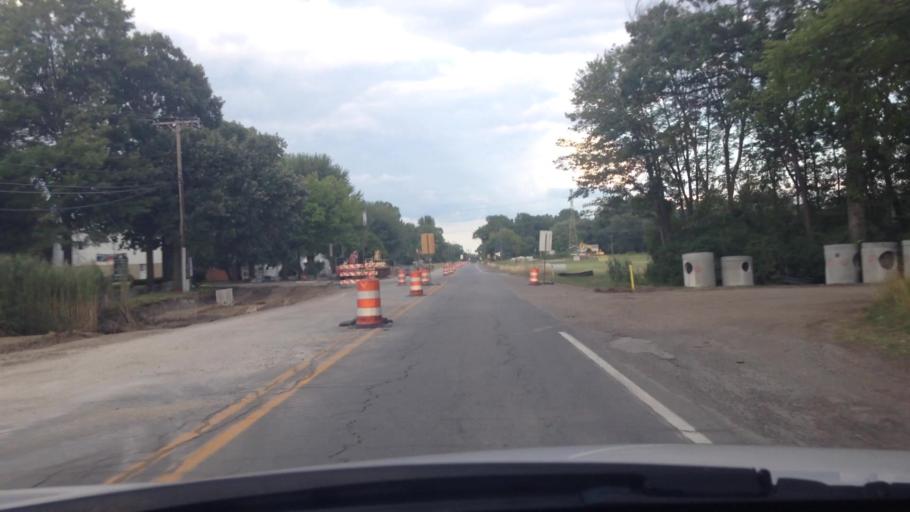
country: US
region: Michigan
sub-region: Wayne County
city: Woodhaven
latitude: 42.1677
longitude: -83.2620
